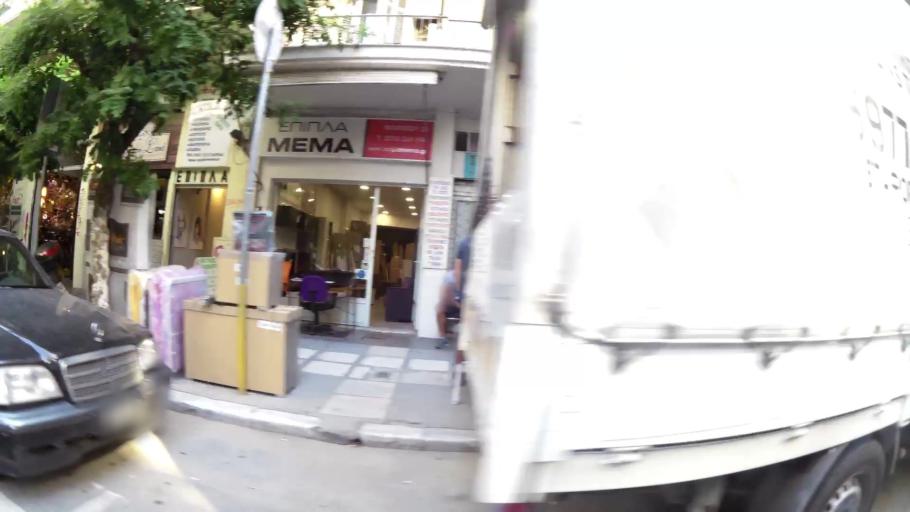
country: GR
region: Central Macedonia
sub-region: Nomos Thessalonikis
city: Sykies
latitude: 40.6381
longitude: 22.9439
